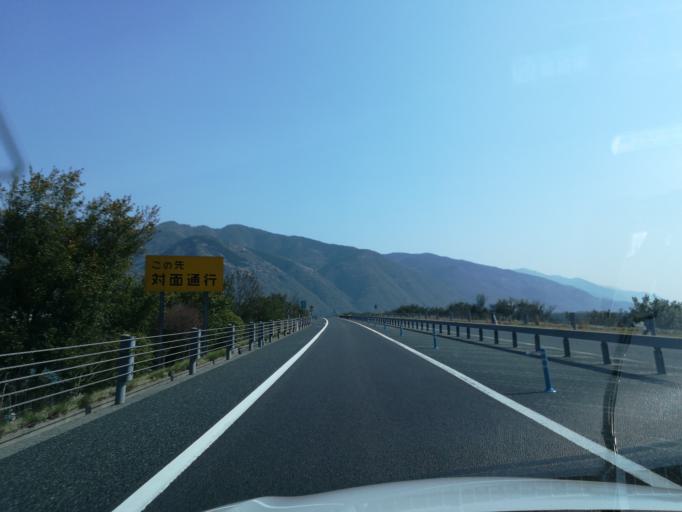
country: JP
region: Tokushima
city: Ikedacho
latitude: 34.0390
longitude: 133.9070
